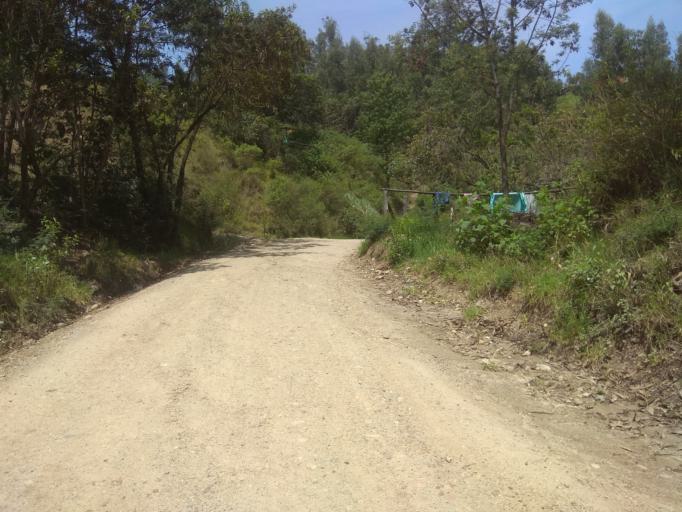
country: CO
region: Boyaca
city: Socha Viejo
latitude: 5.9779
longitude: -72.7296
